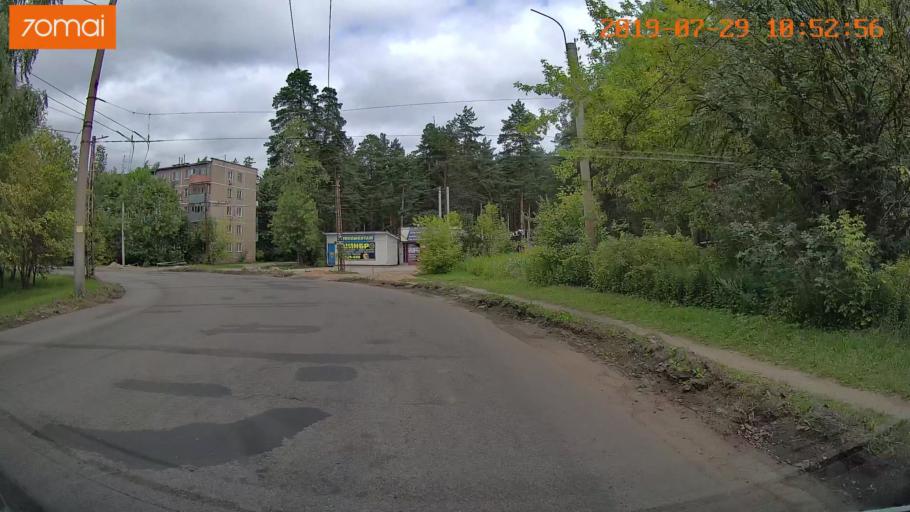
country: RU
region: Ivanovo
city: Kokhma
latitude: 56.9727
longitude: 41.0544
